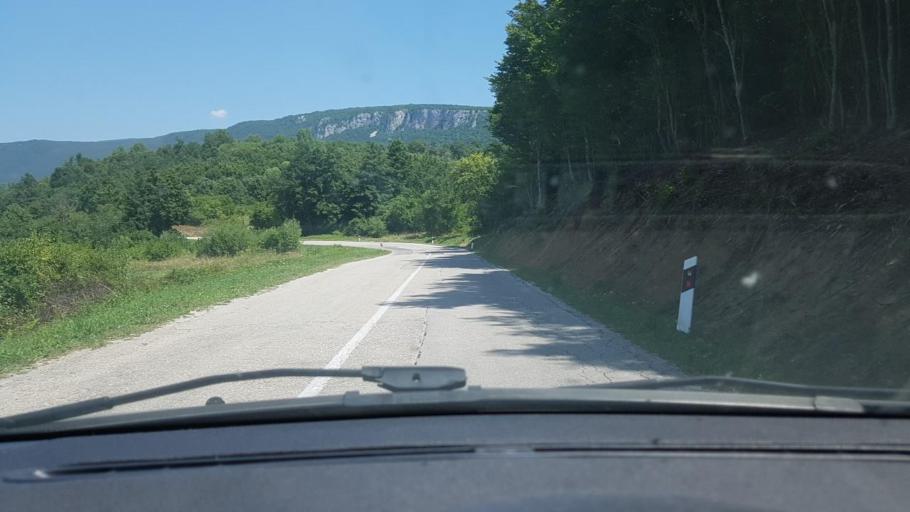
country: BA
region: Federation of Bosnia and Herzegovina
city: Orasac
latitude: 44.5807
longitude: 16.0776
